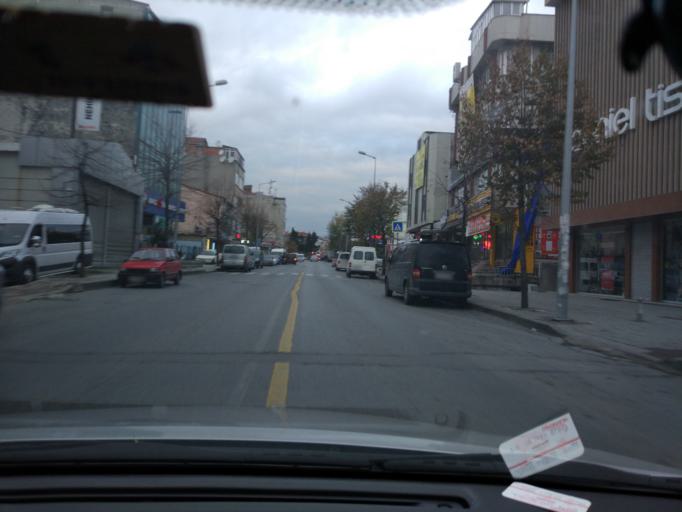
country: TR
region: Istanbul
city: Bahcelievler
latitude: 41.0119
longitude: 28.8271
